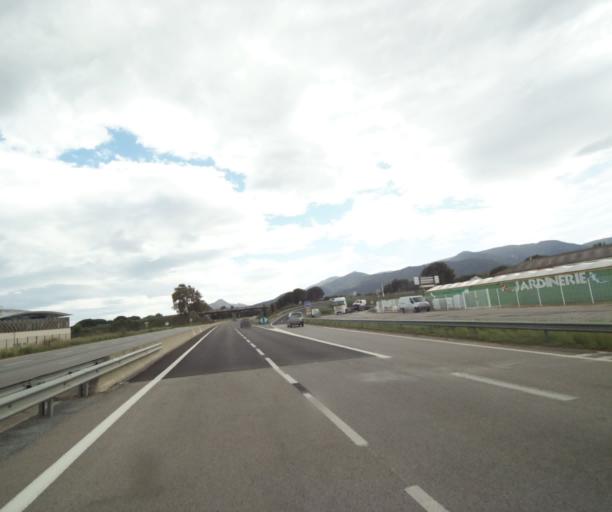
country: FR
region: Languedoc-Roussillon
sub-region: Departement des Pyrenees-Orientales
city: Argelers
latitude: 42.5656
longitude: 3.0038
